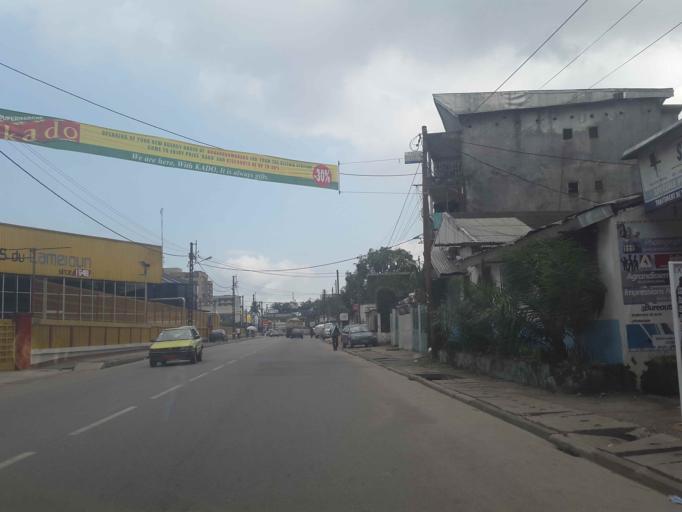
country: CM
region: Littoral
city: Douala
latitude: 4.0332
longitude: 9.6950
